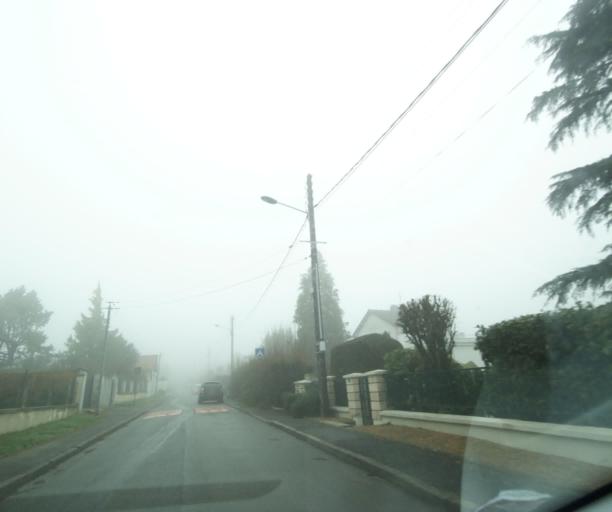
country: FR
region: Ile-de-France
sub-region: Departement de Seine-et-Marne
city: Dammartin-en-Goele
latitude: 49.0510
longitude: 2.6918
